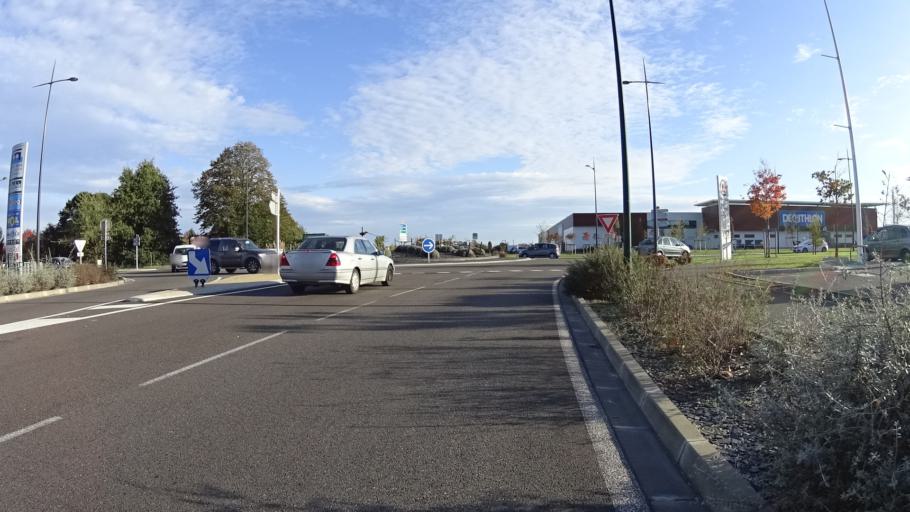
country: FR
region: Aquitaine
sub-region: Departement des Landes
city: Saint-Paul-les-Dax
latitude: 43.7301
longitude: -1.0384
